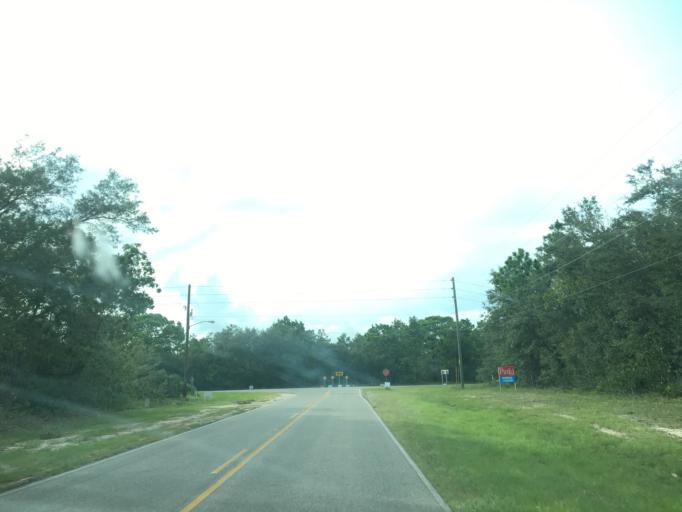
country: US
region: Florida
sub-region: Wakulla County
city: Crawfordville
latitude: 29.9424
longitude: -84.3863
